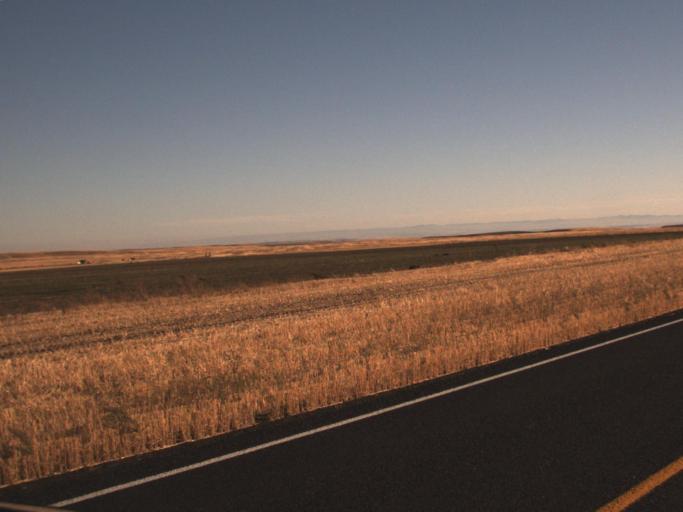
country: US
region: Washington
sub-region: Adams County
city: Ritzville
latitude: 46.8635
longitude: -118.3359
